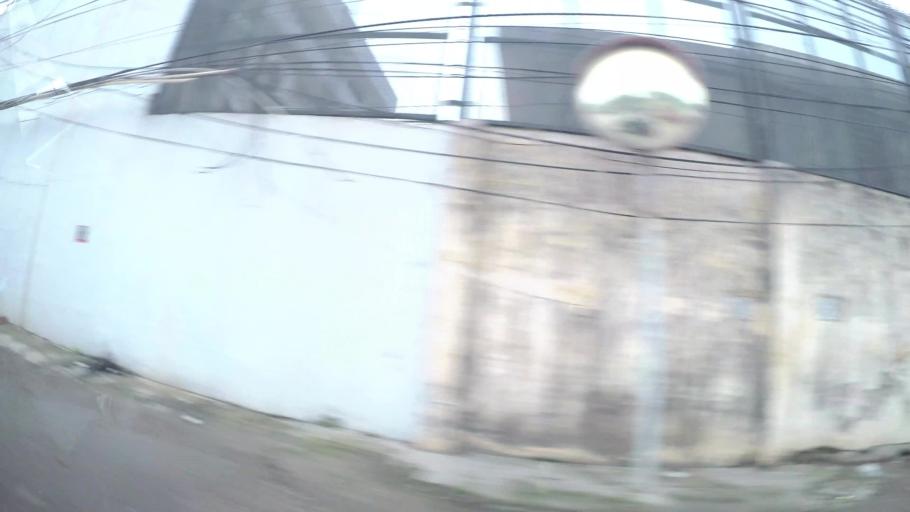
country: VN
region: Ha Noi
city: Hai BaTrung
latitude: 20.9966
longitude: 105.8774
